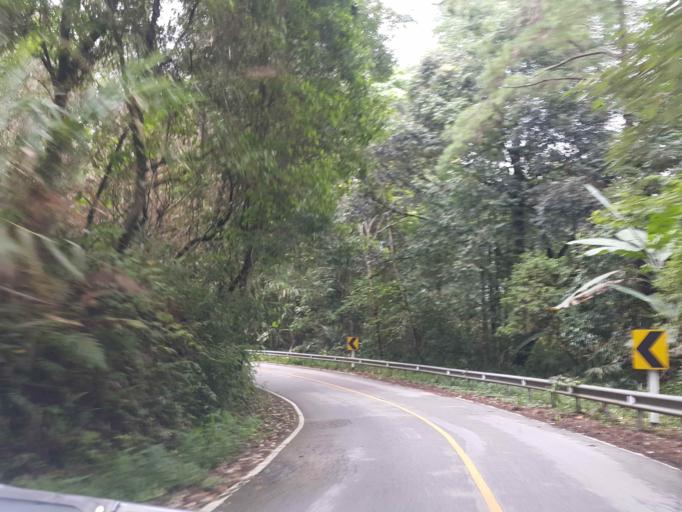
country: TH
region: Chiang Mai
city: Mae Chaem
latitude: 18.5155
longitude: 98.4683
